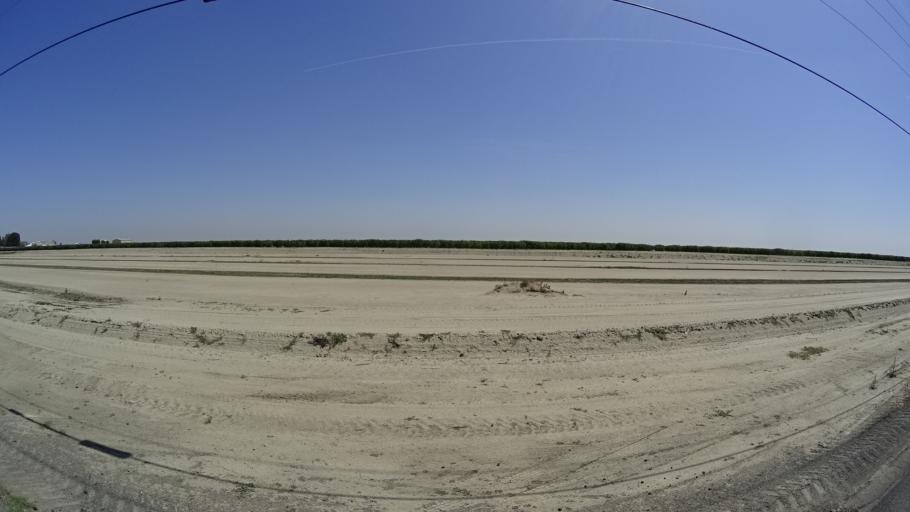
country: US
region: California
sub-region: Kings County
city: Corcoran
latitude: 36.0819
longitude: -119.5447
